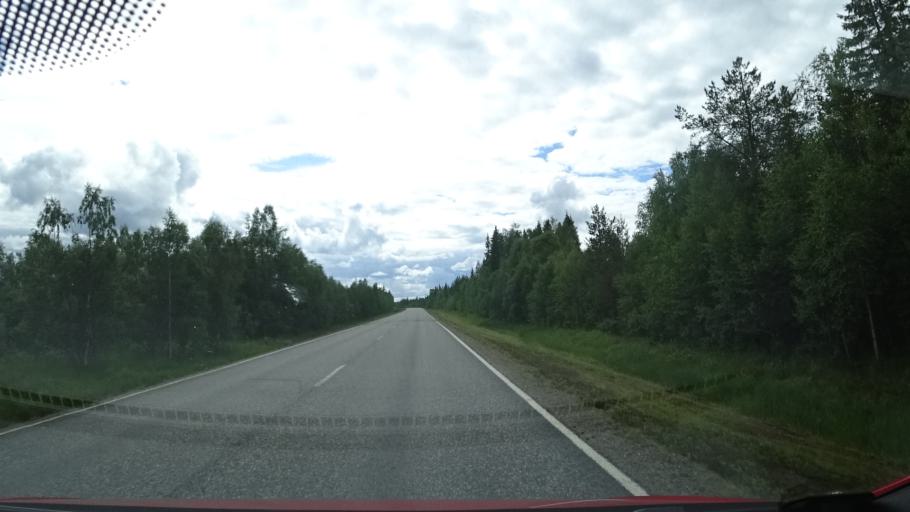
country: FI
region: Lapland
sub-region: Tunturi-Lappi
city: Kittilae
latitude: 67.5421
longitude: 24.9121
